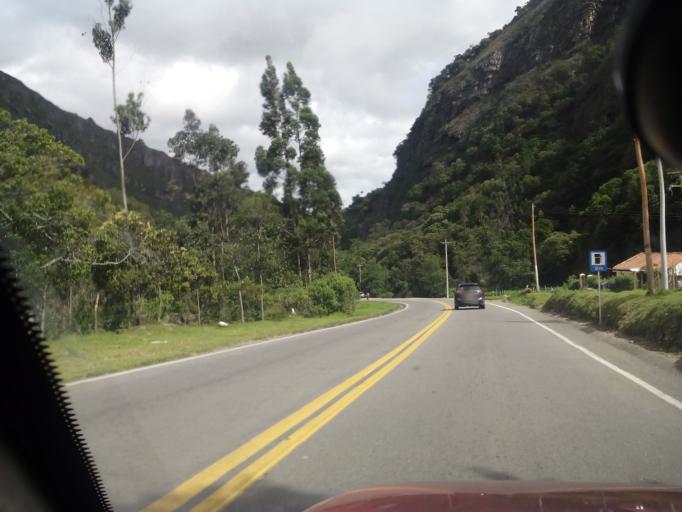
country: CO
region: Boyaca
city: Arcabuco
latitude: 5.7455
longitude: -73.4271
